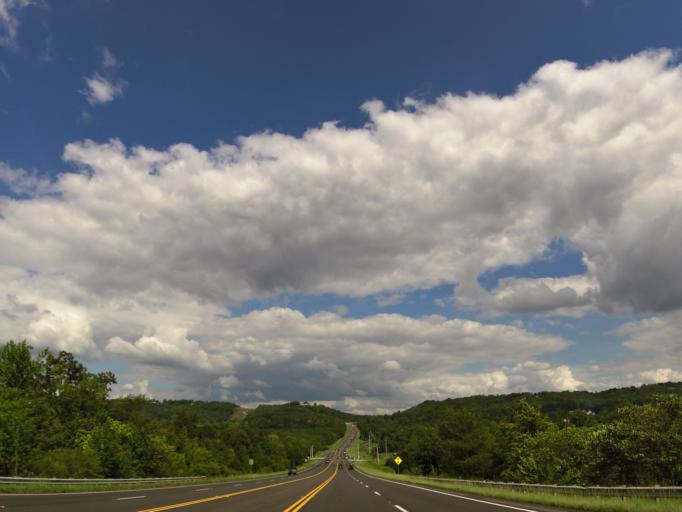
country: US
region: Georgia
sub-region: Walker County
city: Fairview
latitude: 34.9508
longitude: -85.3160
